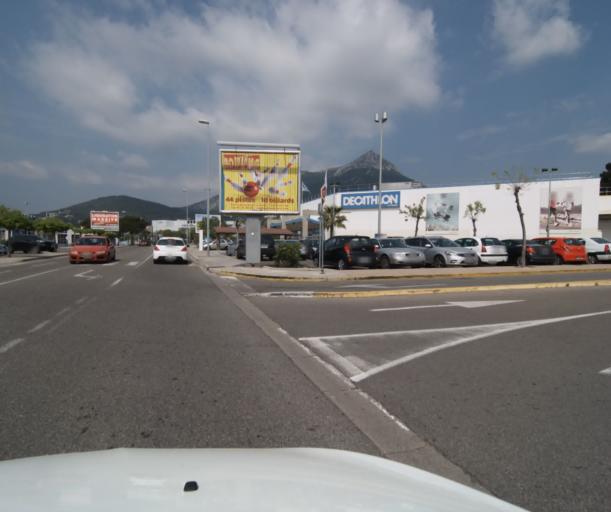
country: FR
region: Provence-Alpes-Cote d'Azur
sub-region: Departement du Var
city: La Garde
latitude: 43.1389
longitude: 6.0213
